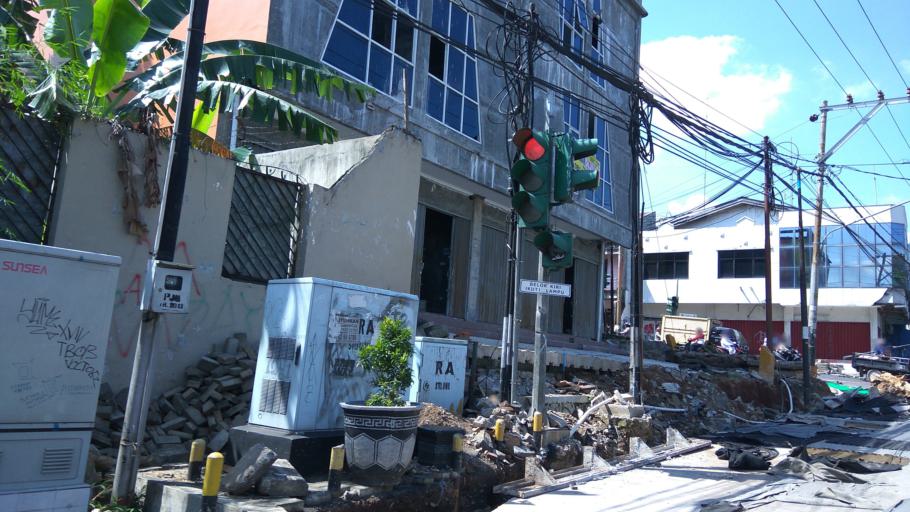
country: ID
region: Central Java
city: Ungaran
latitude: -7.1214
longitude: 110.4089
